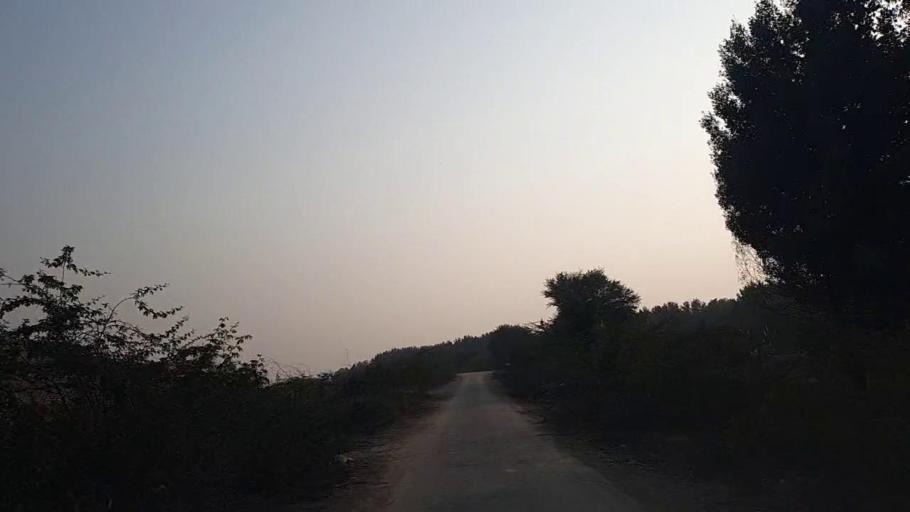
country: PK
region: Sindh
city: Nawabshah
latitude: 26.2390
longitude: 68.4717
